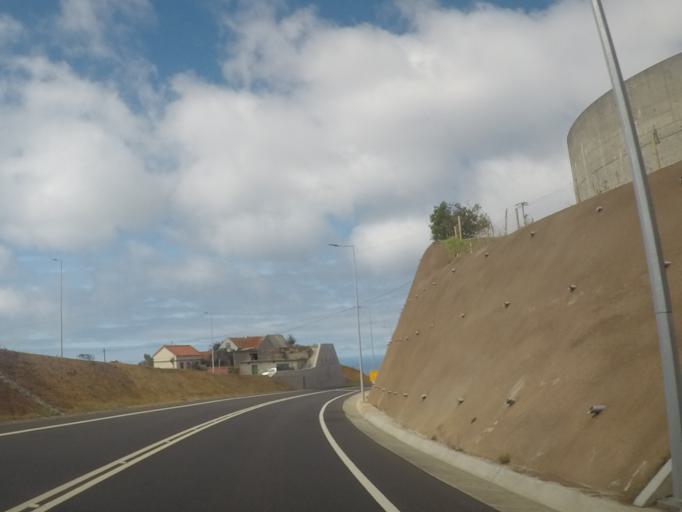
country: PT
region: Madeira
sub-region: Calheta
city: Faja da Ovelha
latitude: 32.8004
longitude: -17.2354
